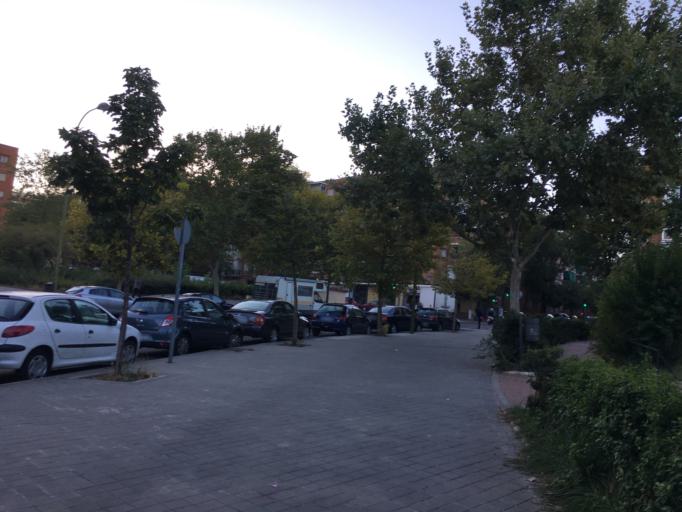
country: ES
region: Madrid
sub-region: Provincia de Madrid
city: Moratalaz
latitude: 40.4307
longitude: -3.6386
